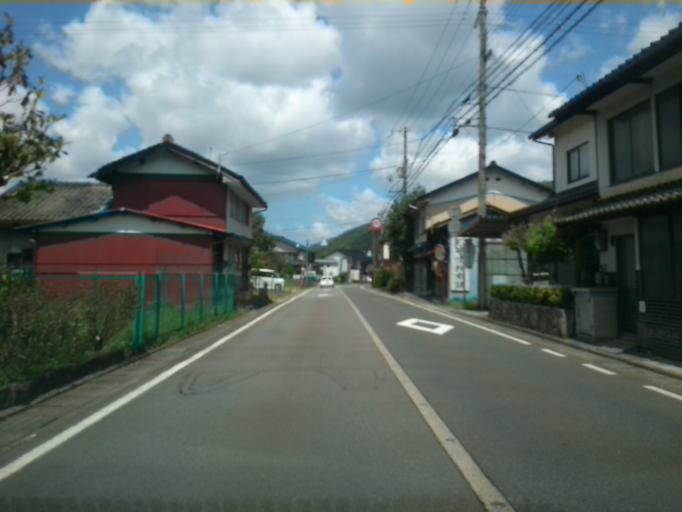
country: JP
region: Hyogo
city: Toyooka
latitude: 35.4587
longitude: 134.8709
